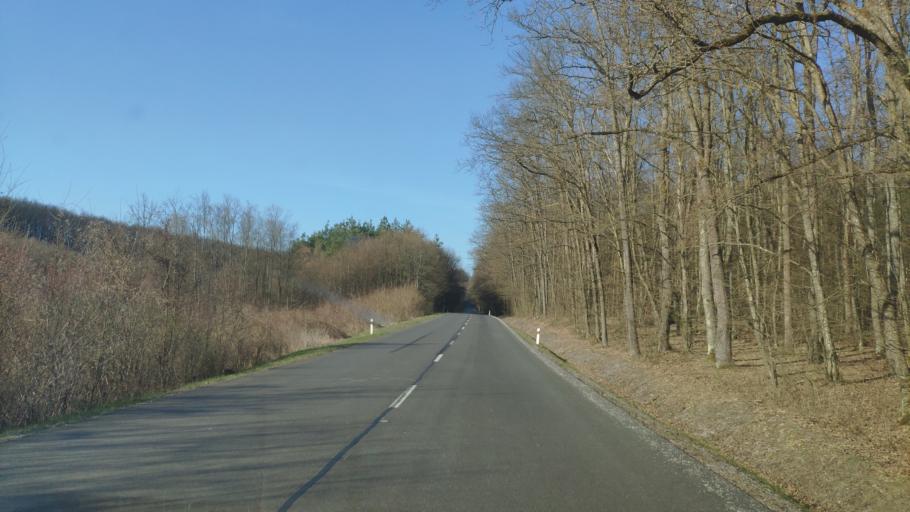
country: HU
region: Borsod-Abauj-Zemplen
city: Putnok
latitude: 48.4982
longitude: 20.2847
